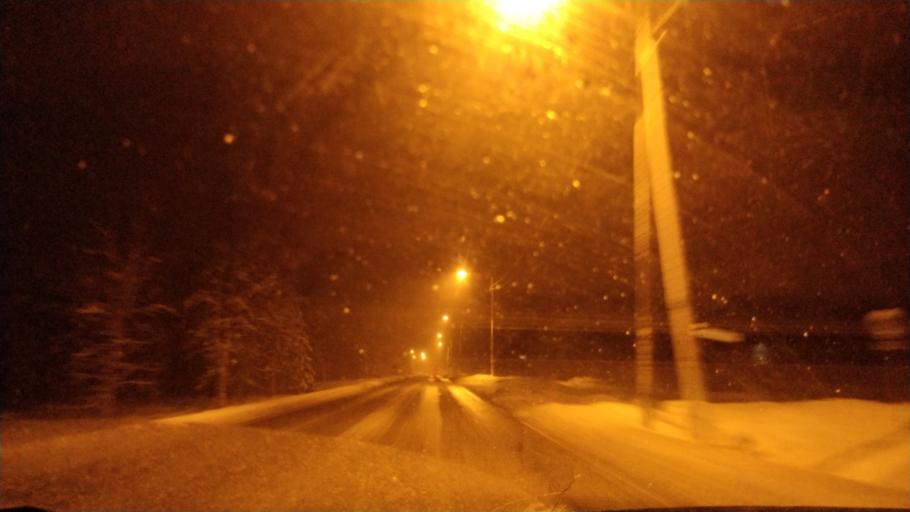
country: FI
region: Lapland
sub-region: Rovaniemi
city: Rovaniemi
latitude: 66.2790
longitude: 25.3341
